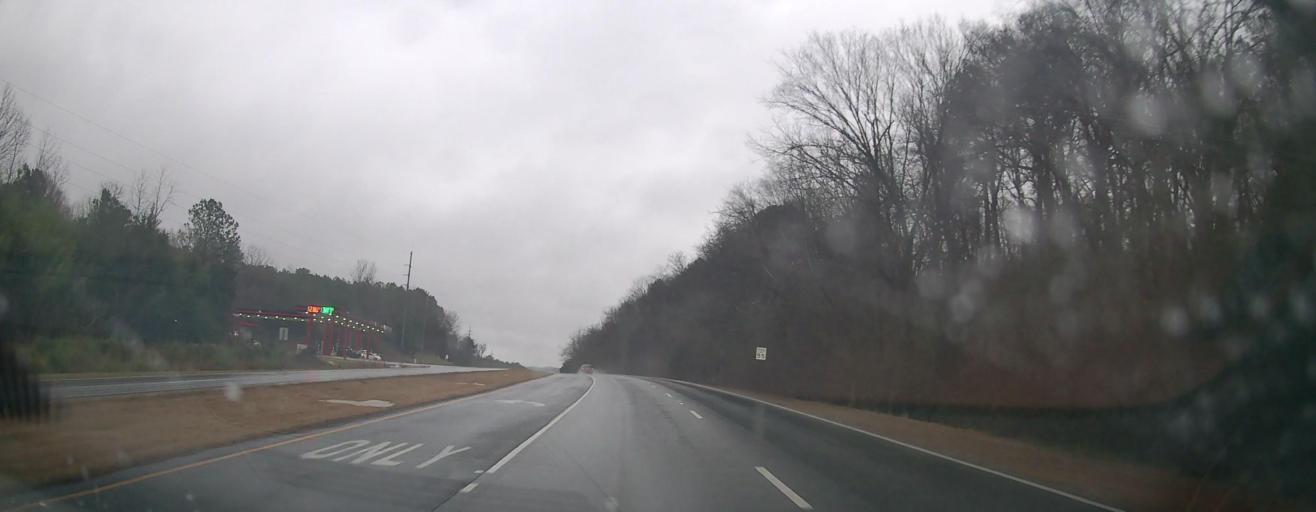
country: US
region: Alabama
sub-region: Morgan County
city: Flint City
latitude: 34.5074
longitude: -86.9695
